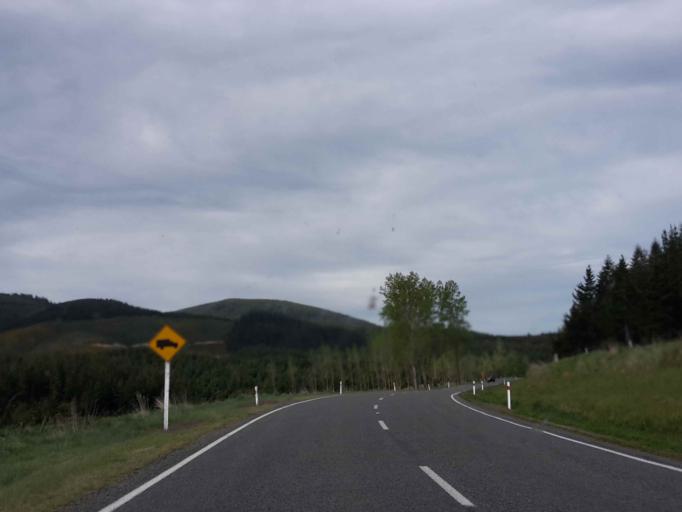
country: NZ
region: Canterbury
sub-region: Timaru District
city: Pleasant Point
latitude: -44.1200
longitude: 171.0547
